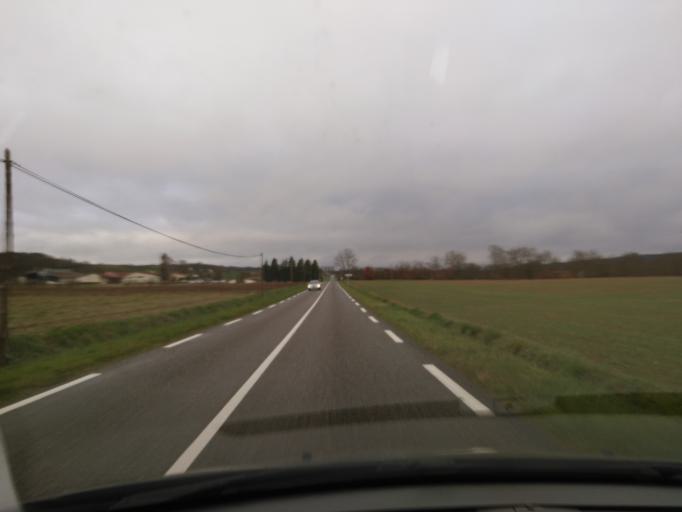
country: FR
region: Midi-Pyrenees
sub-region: Departement de la Haute-Garonne
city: Montesquieu-Volvestre
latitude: 43.1762
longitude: 1.2536
